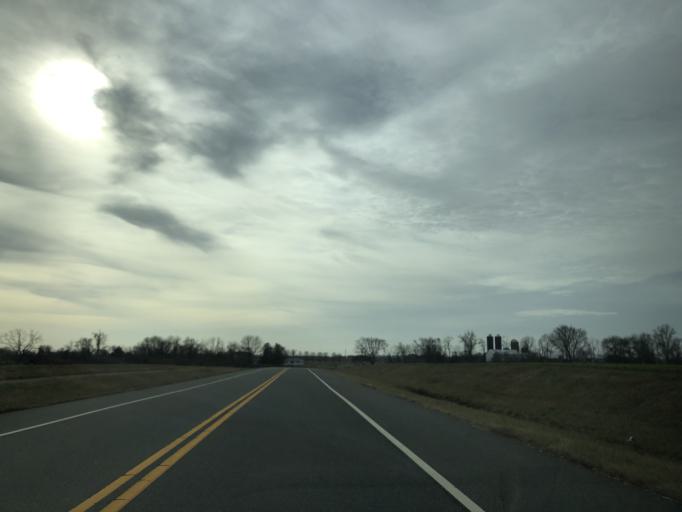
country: US
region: Delaware
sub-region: New Castle County
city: Middletown
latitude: 39.5171
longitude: -75.6789
